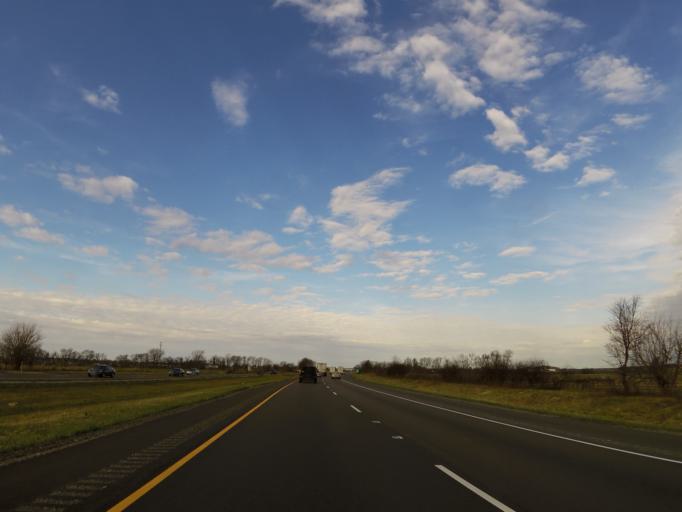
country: US
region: Illinois
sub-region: Washington County
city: Okawville
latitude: 38.4334
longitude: -89.5177
